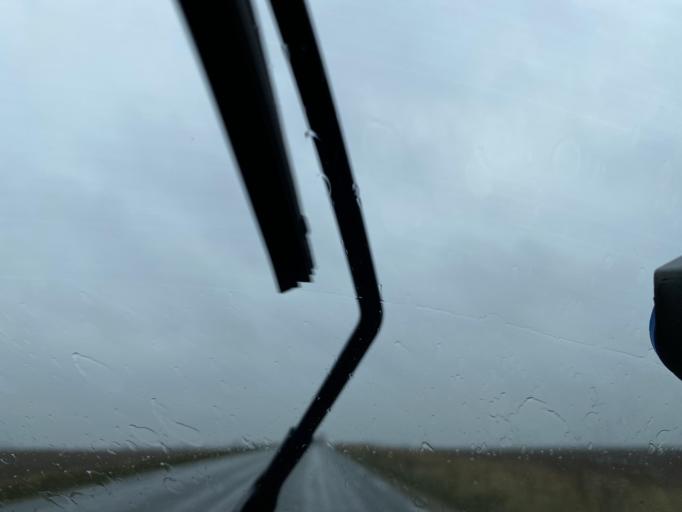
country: FR
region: Centre
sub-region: Departement d'Eure-et-Loir
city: Janville
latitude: 48.2203
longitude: 1.8051
